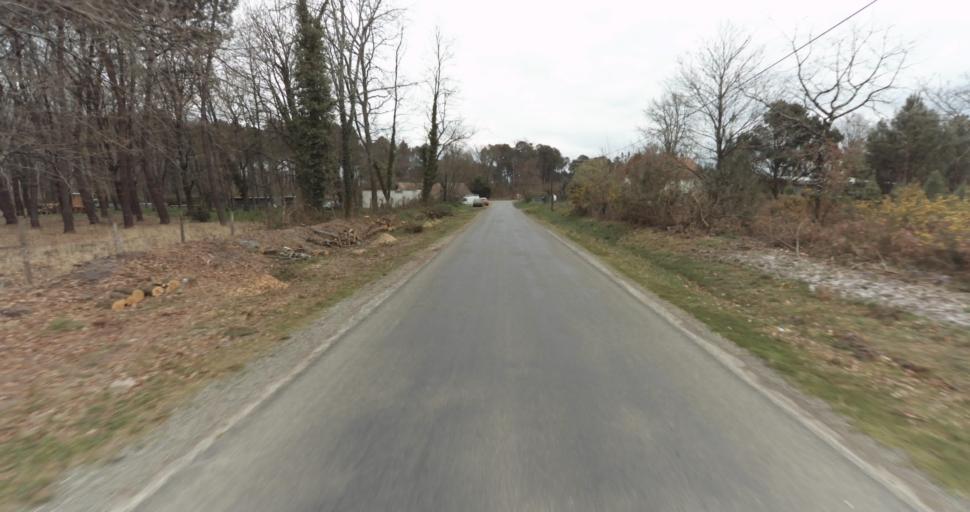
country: FR
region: Aquitaine
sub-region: Departement des Landes
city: Sarbazan
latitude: 44.0098
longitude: -0.3253
